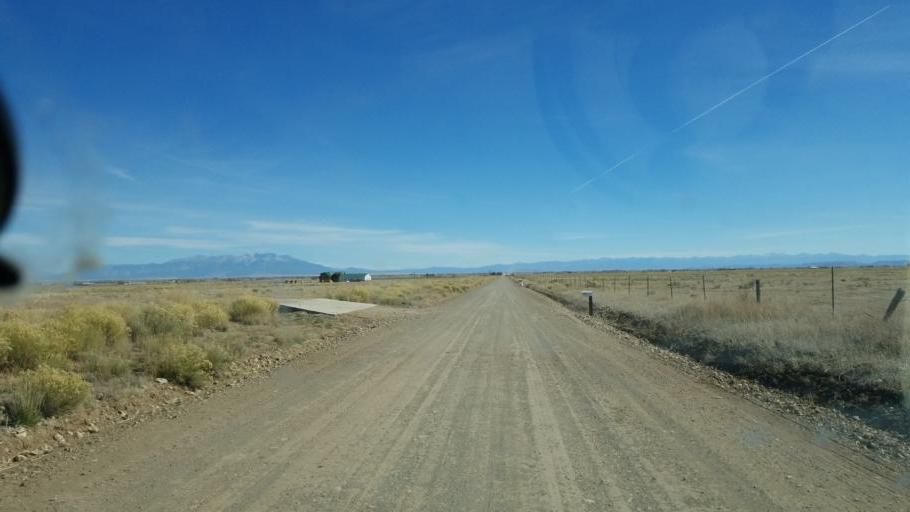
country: US
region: Colorado
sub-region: Rio Grande County
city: Monte Vista
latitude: 37.4011
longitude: -106.1217
